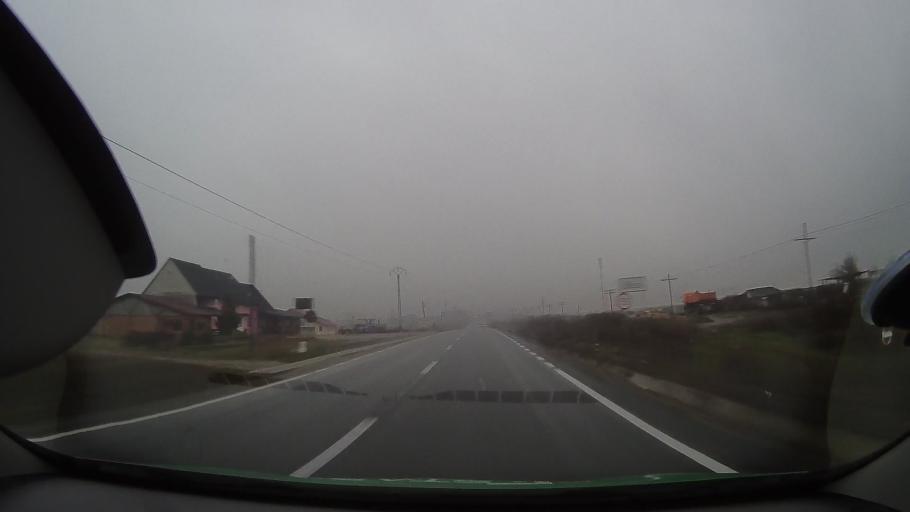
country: RO
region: Bihor
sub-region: Comuna Olcea
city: Olcea
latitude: 46.6893
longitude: 21.9657
